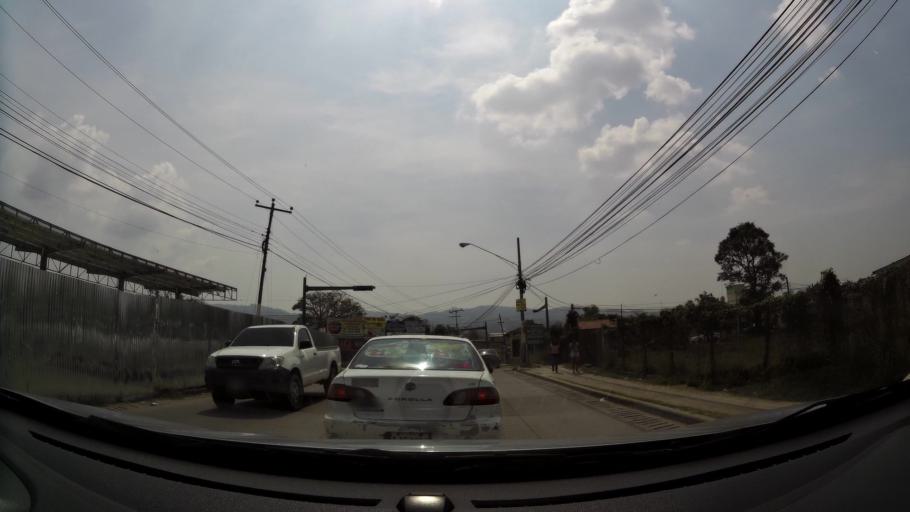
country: HN
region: Comayagua
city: Siguatepeque
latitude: 14.5973
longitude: -87.8351
